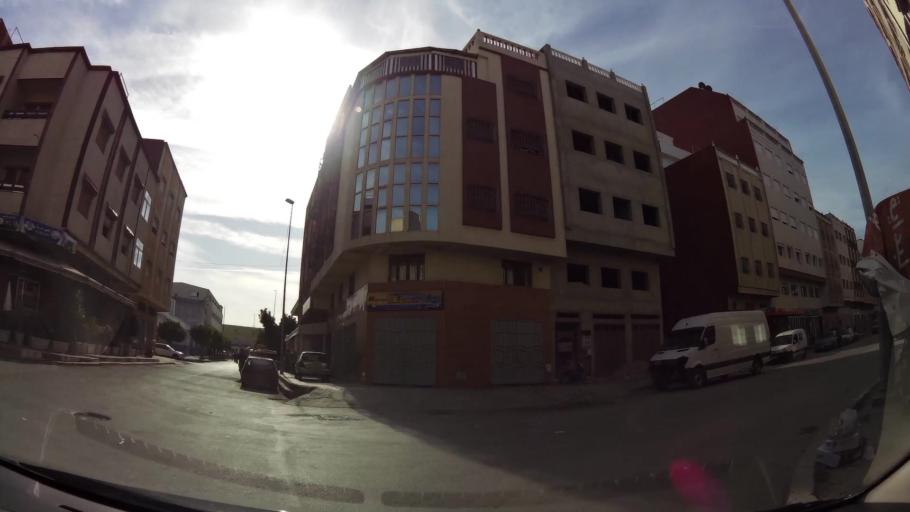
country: MA
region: Tanger-Tetouan
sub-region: Tanger-Assilah
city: Tangier
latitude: 35.7396
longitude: -5.7975
